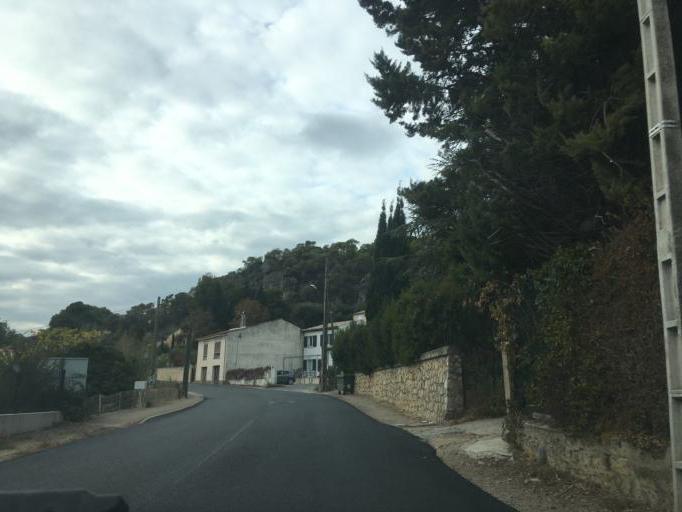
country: FR
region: Provence-Alpes-Cote d'Azur
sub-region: Departement du Var
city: Villecroze
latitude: 43.5837
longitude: 6.2738
